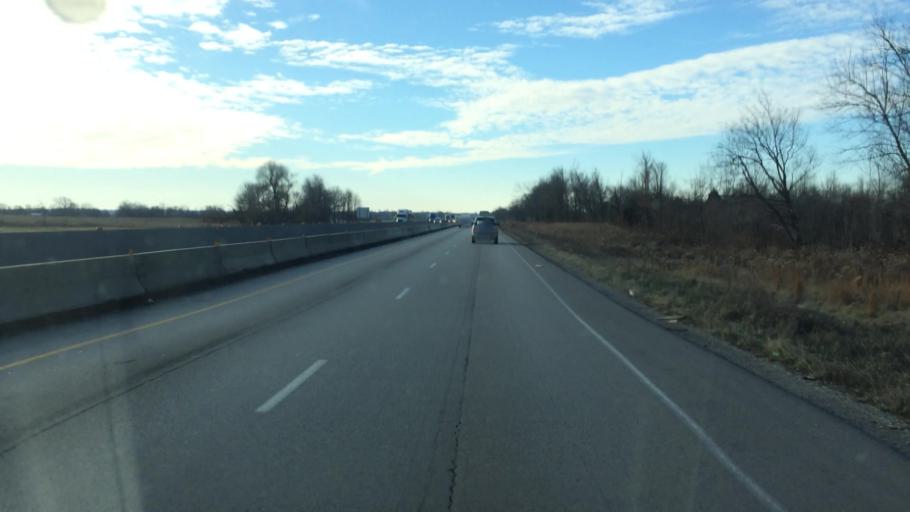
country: US
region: Kentucky
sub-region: Hardin County
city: Elizabethtown
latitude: 37.5906
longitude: -85.8701
